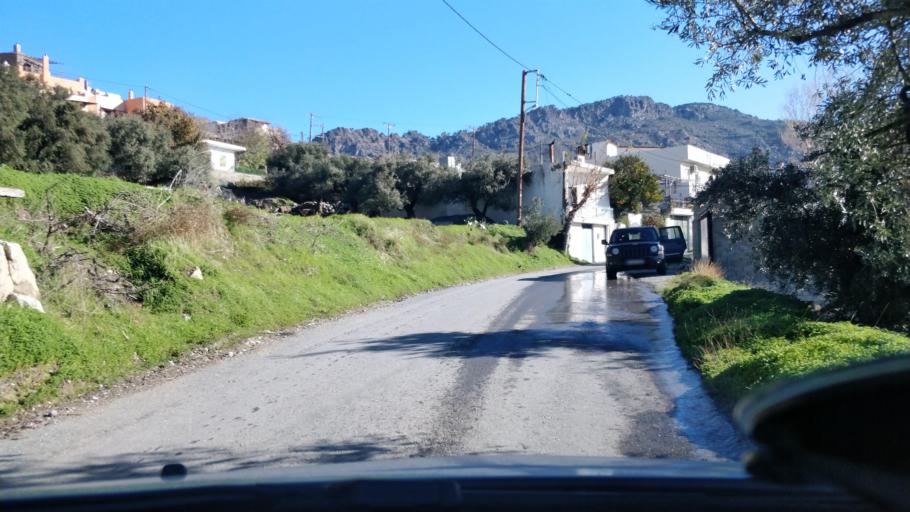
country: GR
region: Crete
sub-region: Nomos Lasithiou
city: Kritsa
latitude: 35.0793
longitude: 25.5835
